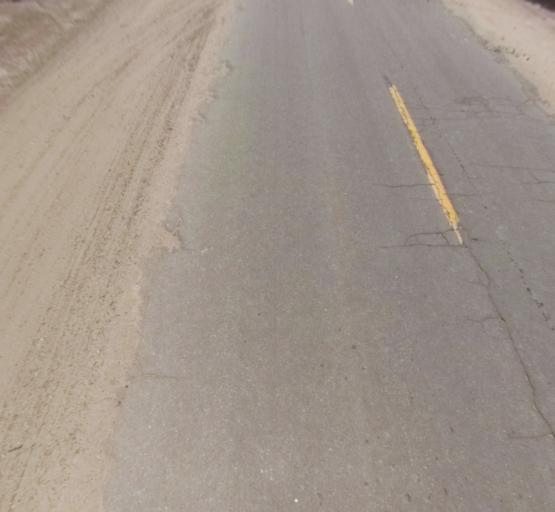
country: US
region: California
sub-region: Madera County
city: Chowchilla
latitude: 37.0983
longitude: -120.4112
